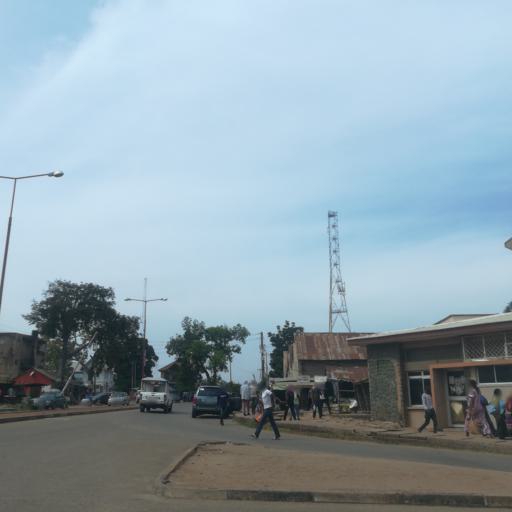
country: NG
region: Plateau
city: Jos
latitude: 9.9140
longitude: 8.8898
